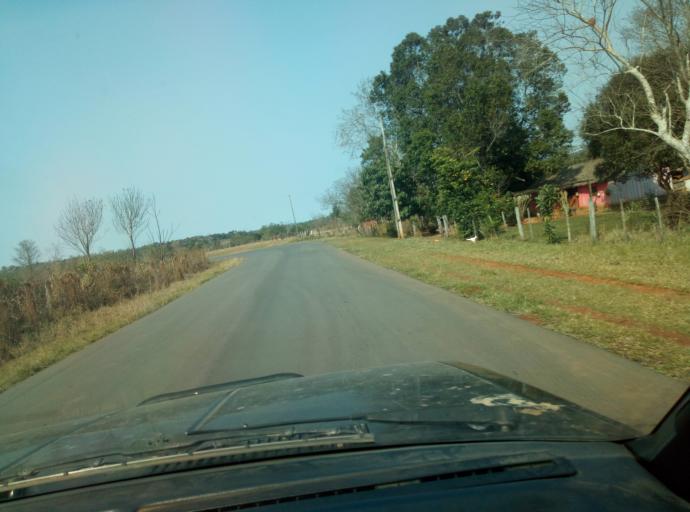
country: PY
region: Caaguazu
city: Carayao
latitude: -25.2629
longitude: -56.2879
